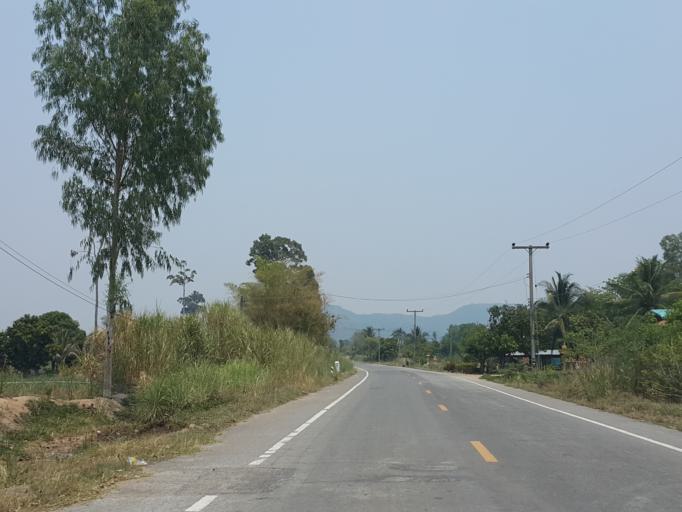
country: TH
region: Kamphaeng Phet
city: Pang Sila Thong
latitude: 16.0549
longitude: 99.3588
